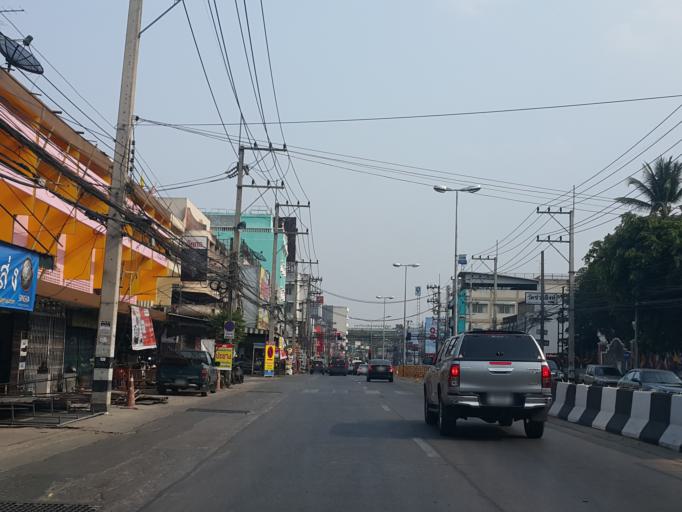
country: TH
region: Chiang Mai
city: Chiang Mai
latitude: 18.8135
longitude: 98.9836
